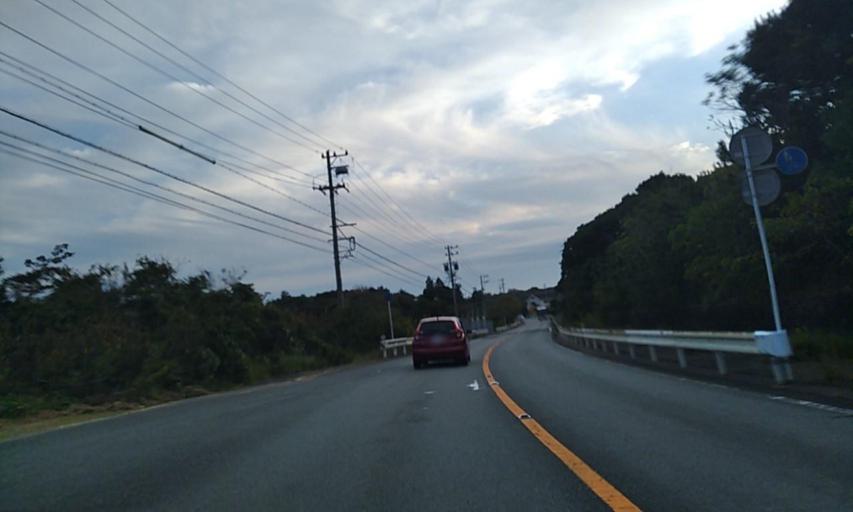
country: JP
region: Mie
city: Toba
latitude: 34.3021
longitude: 136.8761
